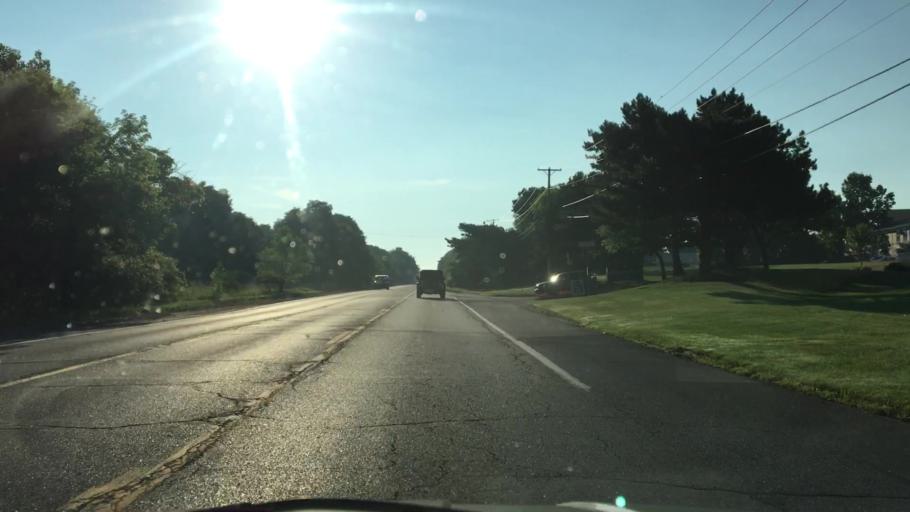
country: US
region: Michigan
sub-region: Oakland County
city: South Lyon
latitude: 42.5166
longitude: -83.6490
